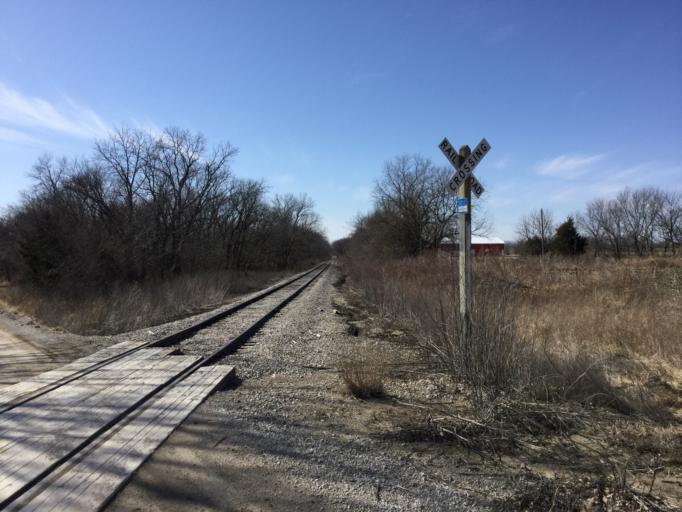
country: US
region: Kansas
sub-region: Douglas County
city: Baldwin City
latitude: 38.7296
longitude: -95.2418
